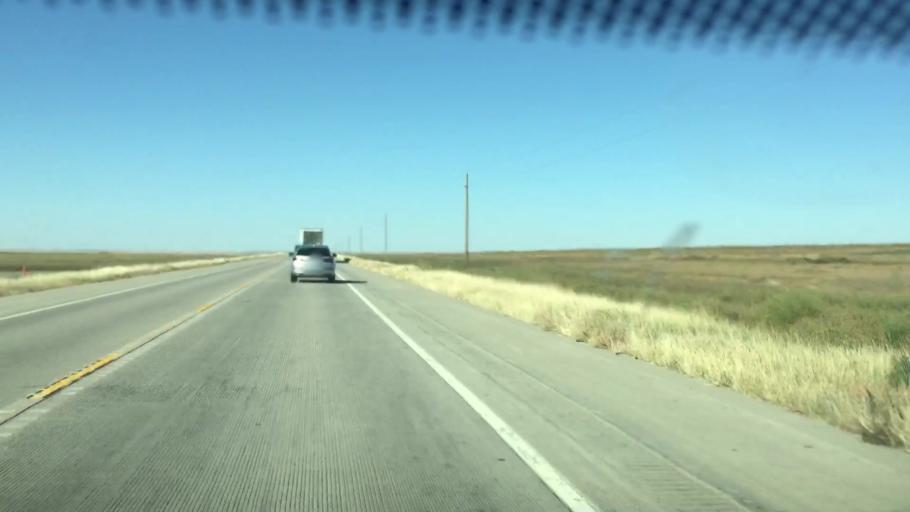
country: US
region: Colorado
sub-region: Kiowa County
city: Eads
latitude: 38.3095
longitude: -102.7199
